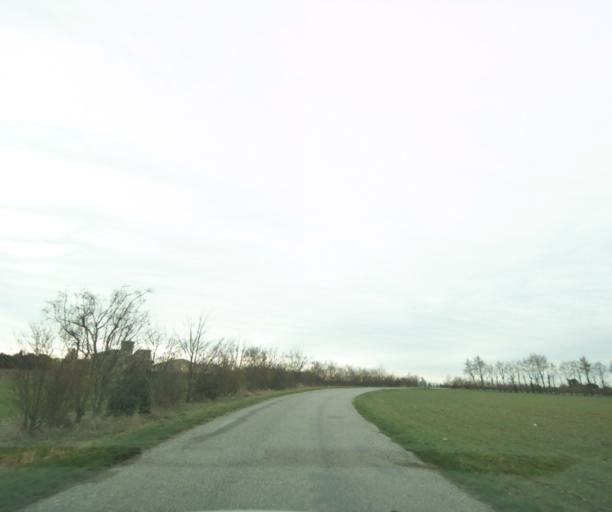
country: FR
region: Rhone-Alpes
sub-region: Departement de la Drome
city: Bourg-les-Valence
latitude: 44.9722
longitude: 4.9057
